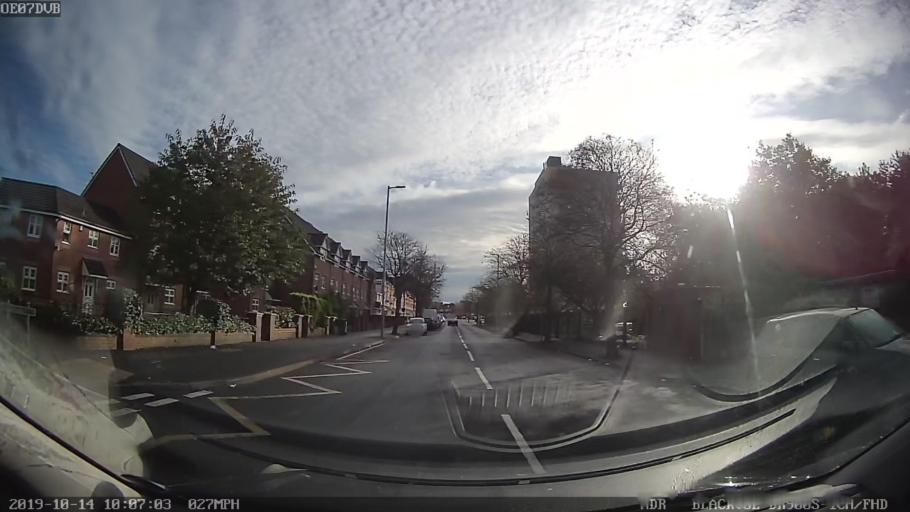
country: GB
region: England
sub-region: Manchester
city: Failsworth
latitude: 53.5227
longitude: -2.1856
